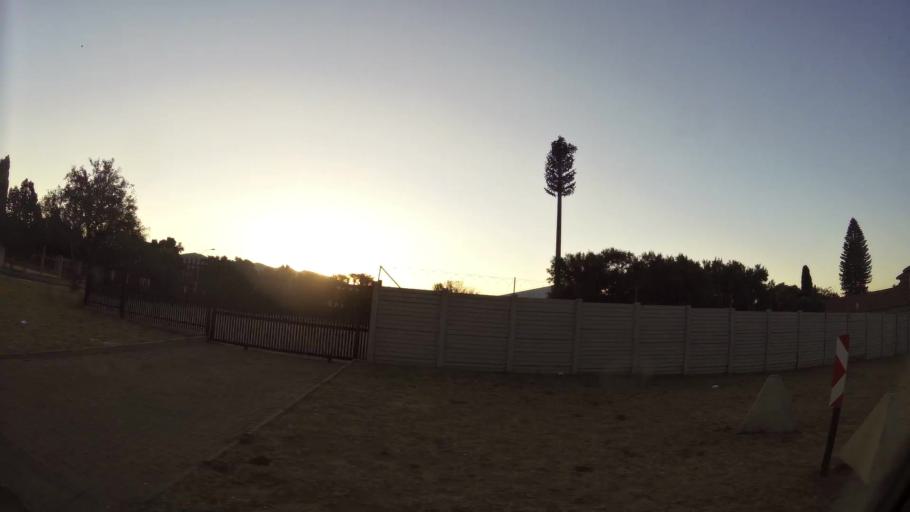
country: ZA
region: North-West
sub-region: Bojanala Platinum District Municipality
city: Rustenburg
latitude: -25.6636
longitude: 27.2170
